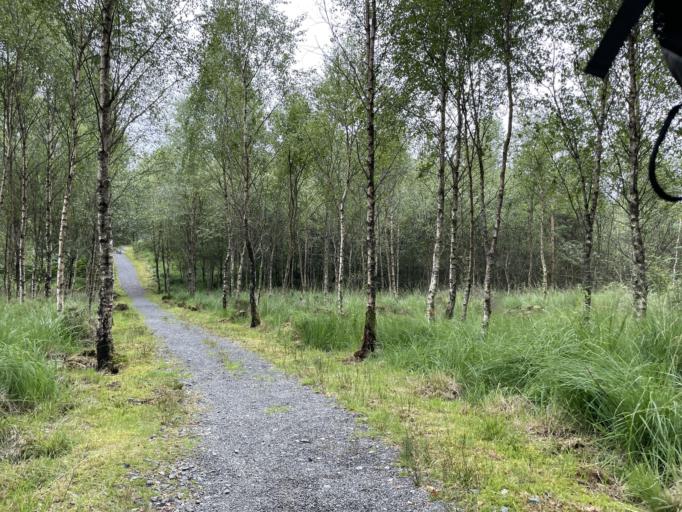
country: GB
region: Scotland
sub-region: Dumfries and Galloway
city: Newton Stewart
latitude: 55.0820
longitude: -4.5091
